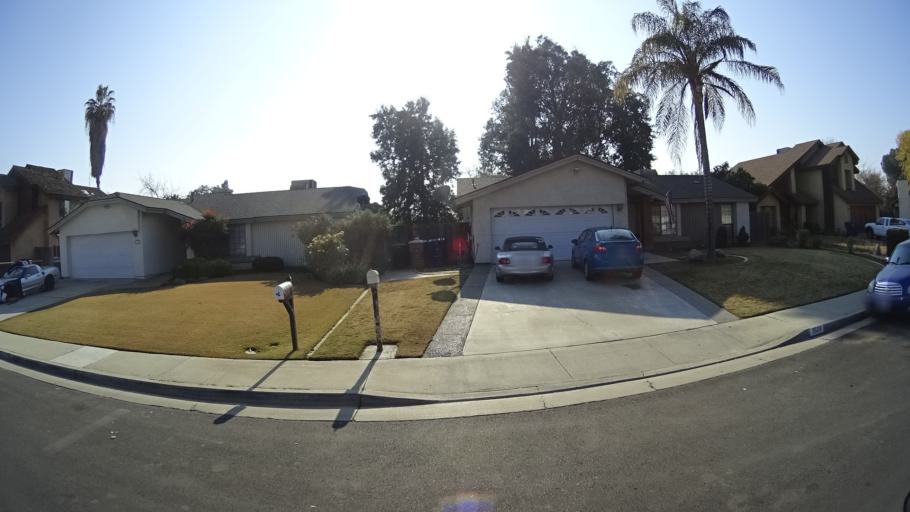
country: US
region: California
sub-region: Kern County
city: Greenacres
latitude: 35.3221
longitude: -119.0848
